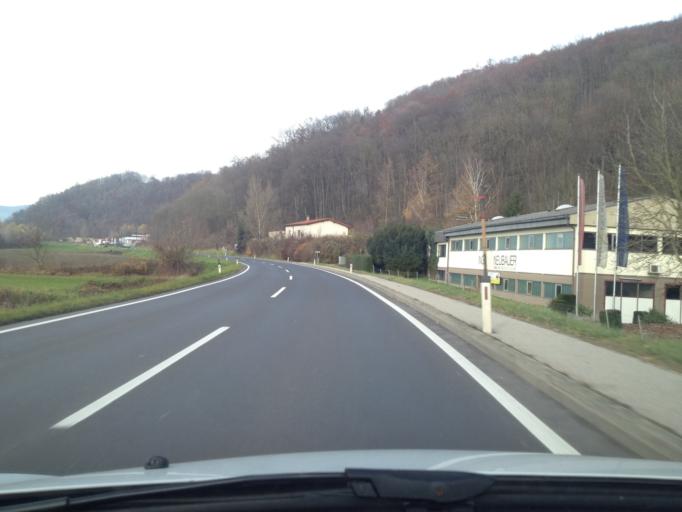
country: AT
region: Upper Austria
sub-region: Politischer Bezirk Urfahr-Umgebung
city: Steyregg
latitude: 48.2979
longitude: 14.3429
